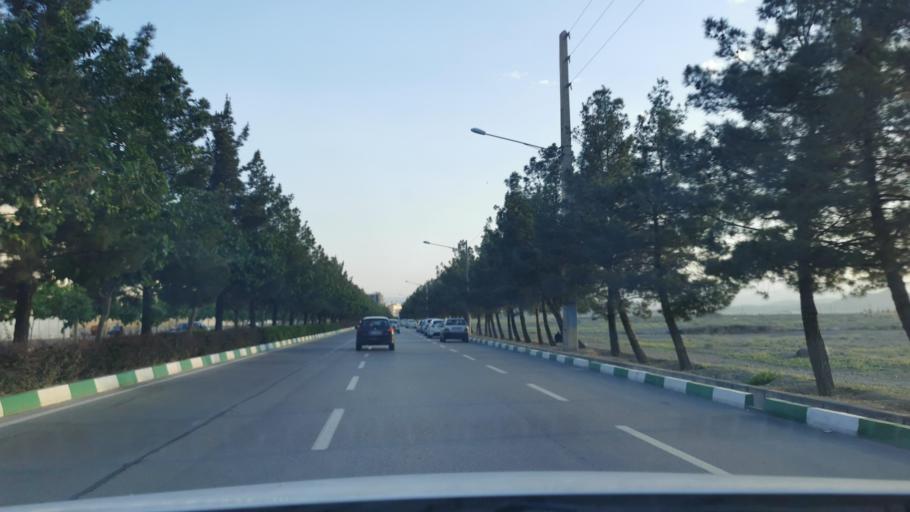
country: IR
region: Razavi Khorasan
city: Torqabeh
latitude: 36.3849
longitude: 59.4644
